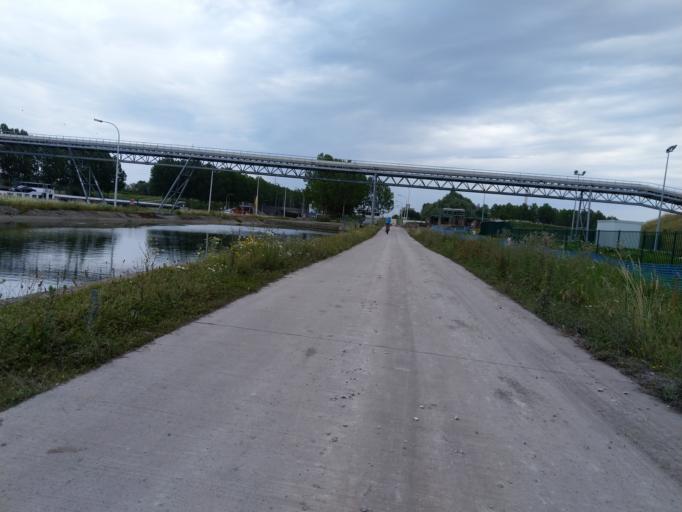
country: BE
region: Wallonia
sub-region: Province du Hainaut
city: Mons
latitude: 50.4806
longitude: 3.9762
